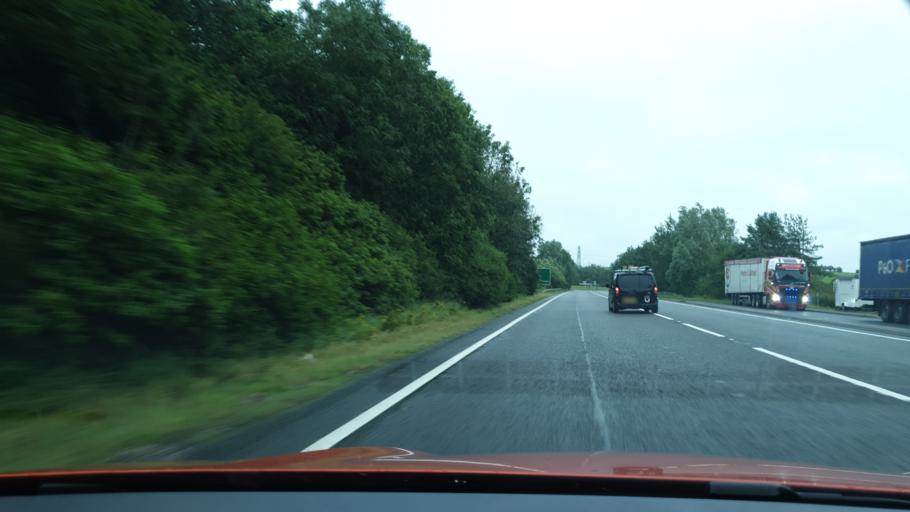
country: GB
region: England
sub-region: Cumbria
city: Dalton in Furness
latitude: 54.1653
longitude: -3.1688
